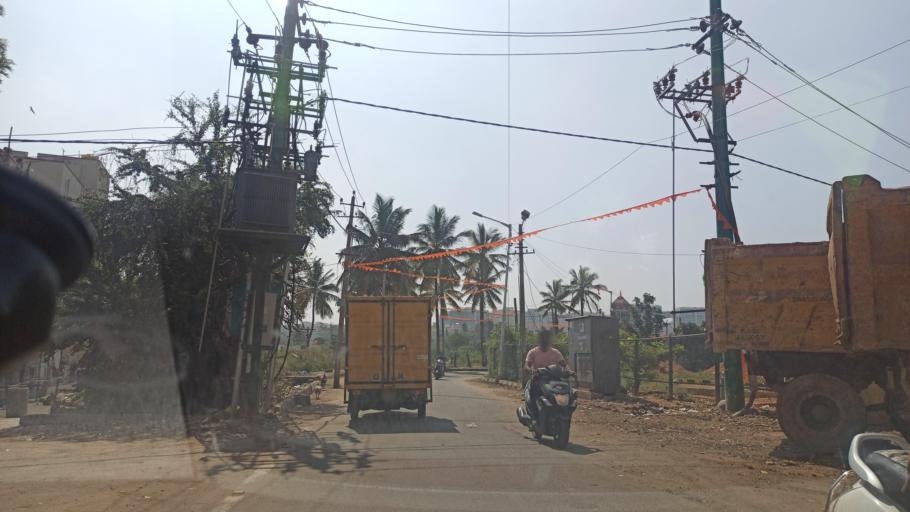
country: IN
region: Karnataka
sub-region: Bangalore Urban
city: Yelahanka
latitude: 13.0635
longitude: 77.6007
